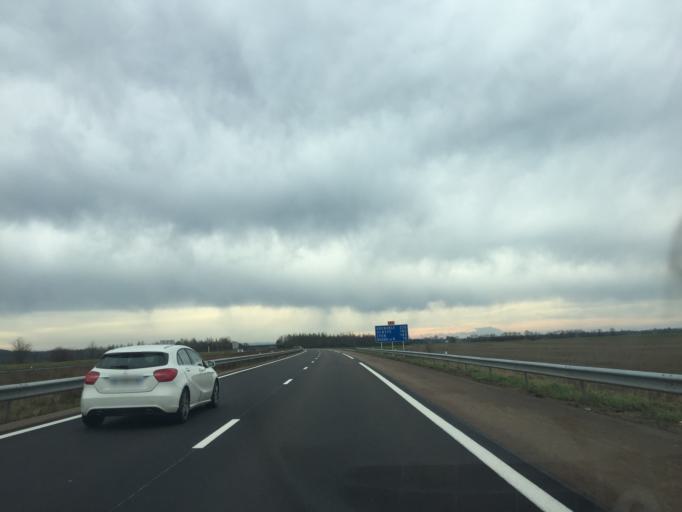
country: FR
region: Franche-Comte
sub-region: Departement du Jura
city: Bletterans
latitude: 46.7655
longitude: 5.5114
